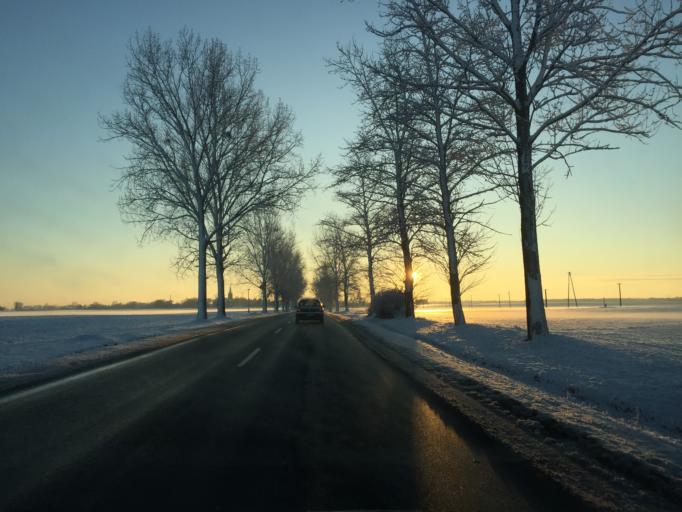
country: PL
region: Kujawsko-Pomorskie
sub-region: Powiat golubsko-dobrzynski
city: Kowalewo Pomorskie
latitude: 53.1269
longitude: 18.8403
